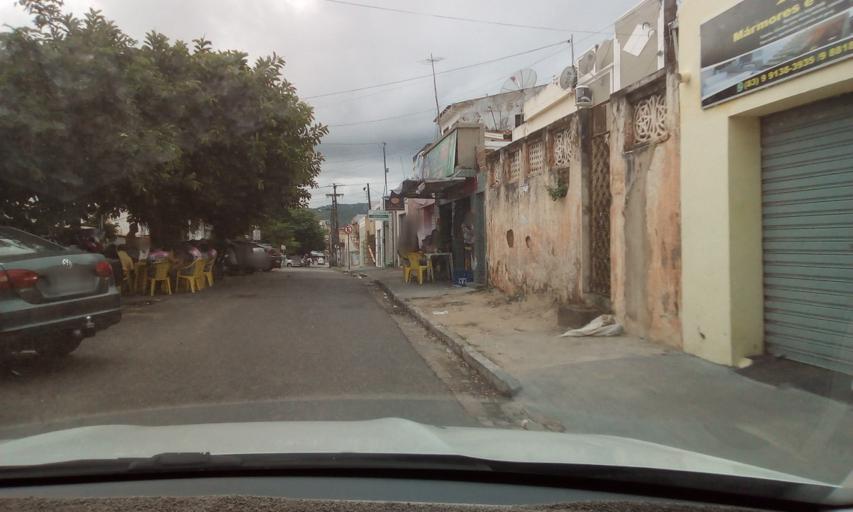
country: BR
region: Paraiba
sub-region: Guarabira
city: Guarabira
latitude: -6.8522
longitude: -35.4892
